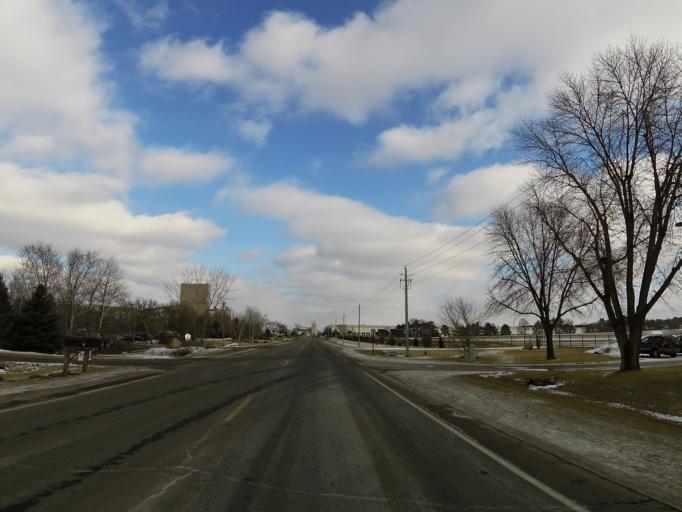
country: US
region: Minnesota
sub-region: Scott County
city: Shakopee
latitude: 44.7975
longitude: -93.4853
